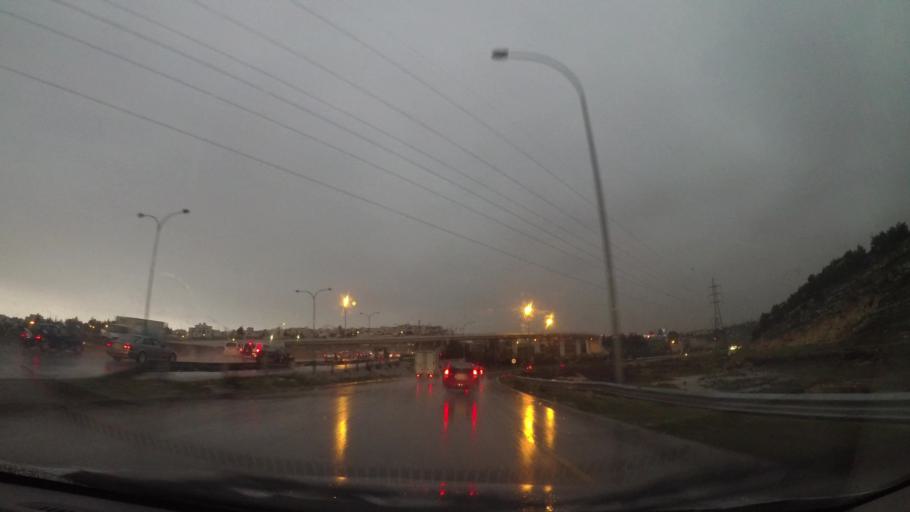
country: JO
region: Amman
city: Umm as Summaq
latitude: 31.9115
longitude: 35.8600
